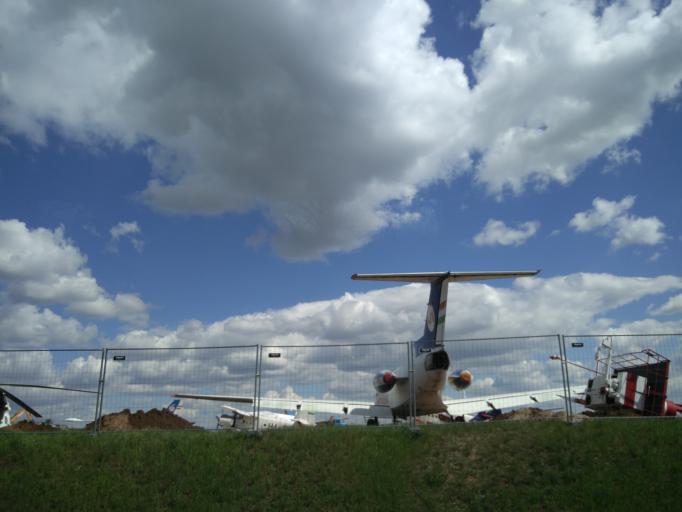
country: HU
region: Pest
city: Vecses
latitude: 47.4242
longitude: 19.2616
